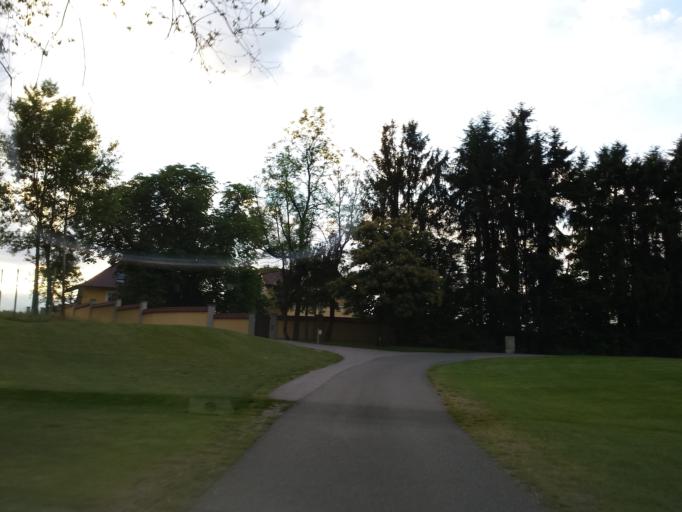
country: AT
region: Styria
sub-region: Politischer Bezirk Graz-Umgebung
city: Thal
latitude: 47.0679
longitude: 15.3623
